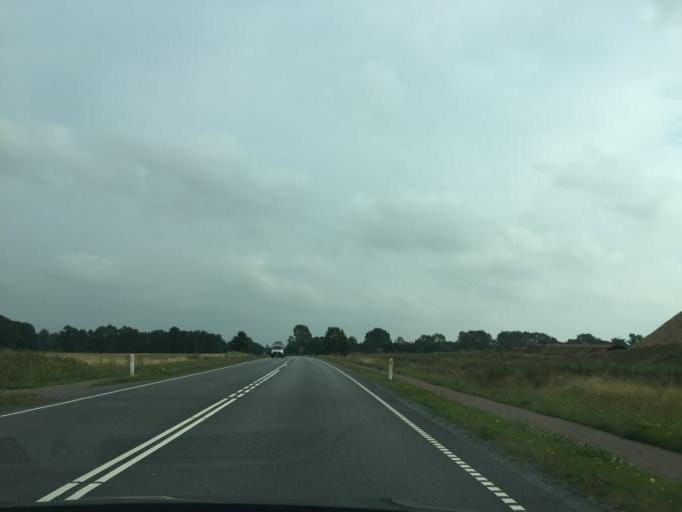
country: DK
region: South Denmark
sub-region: Odense Kommune
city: Hojby
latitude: 55.3276
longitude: 10.3970
